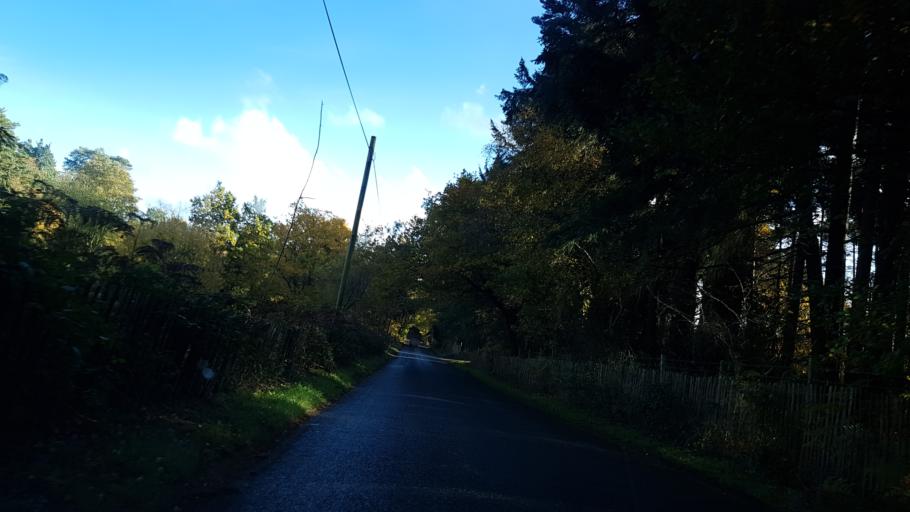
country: GB
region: England
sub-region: Surrey
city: Churt
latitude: 51.1477
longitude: -0.7510
